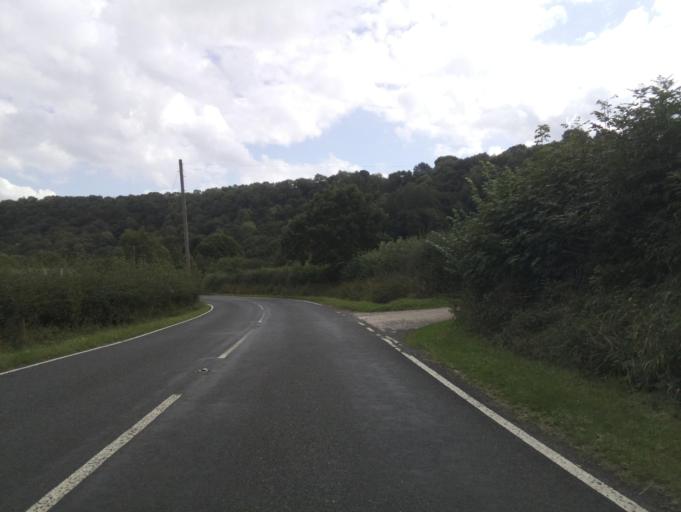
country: GB
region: England
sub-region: North Yorkshire
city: Catterick Garrison
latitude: 54.4024
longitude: -1.7795
